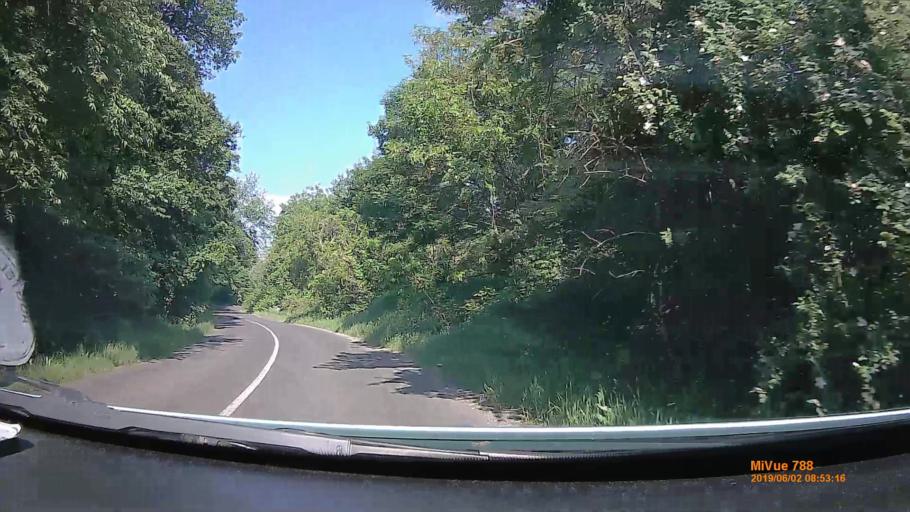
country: HU
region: Borsod-Abauj-Zemplen
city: Sajobabony
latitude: 48.1510
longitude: 20.6826
